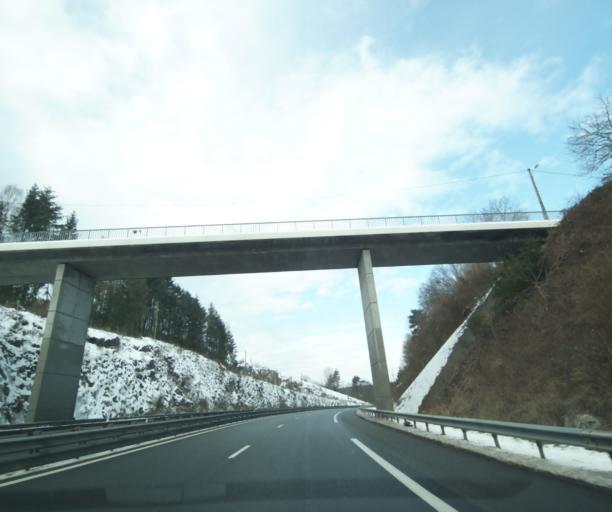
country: FR
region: Auvergne
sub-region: Departement du Puy-de-Dome
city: Saint-Remy-sur-Durolle
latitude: 45.8820
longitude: 3.5926
